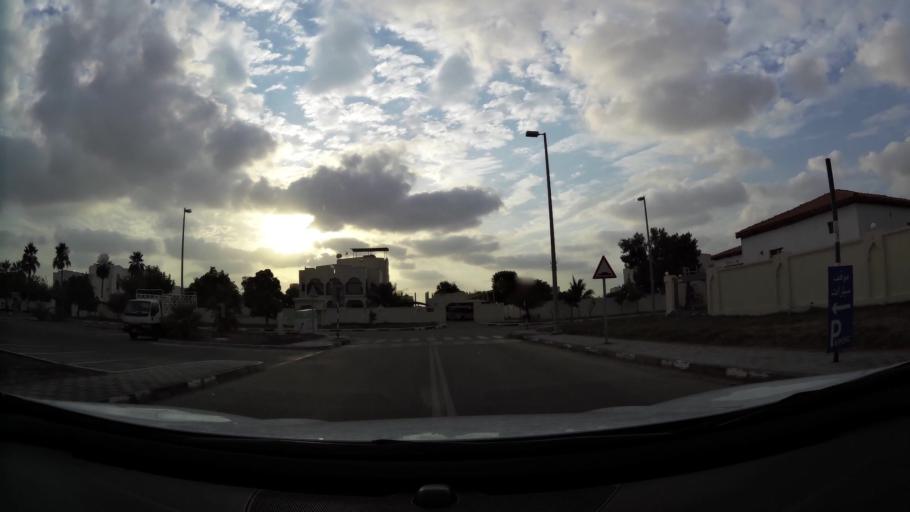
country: AE
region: Abu Dhabi
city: Abu Dhabi
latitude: 24.3862
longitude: 54.5309
